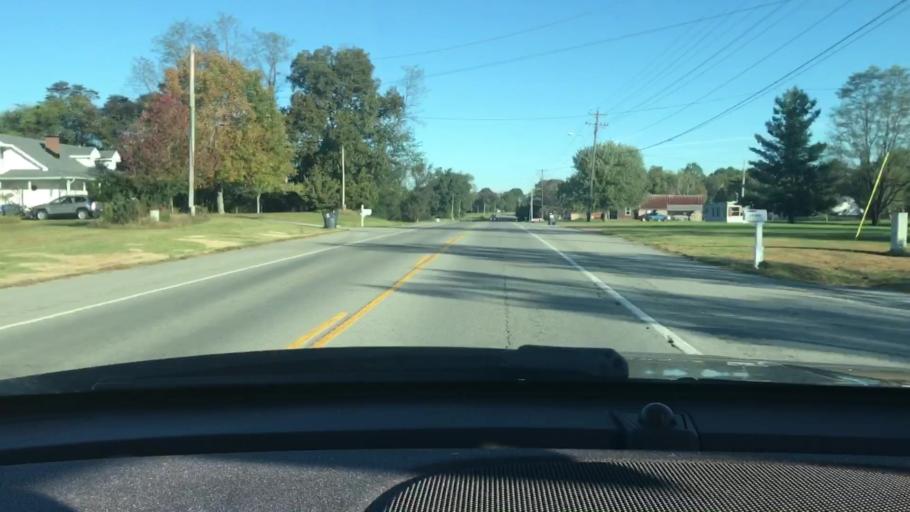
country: US
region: Tennessee
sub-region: Sumner County
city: Millersville
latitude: 36.4136
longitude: -86.6927
